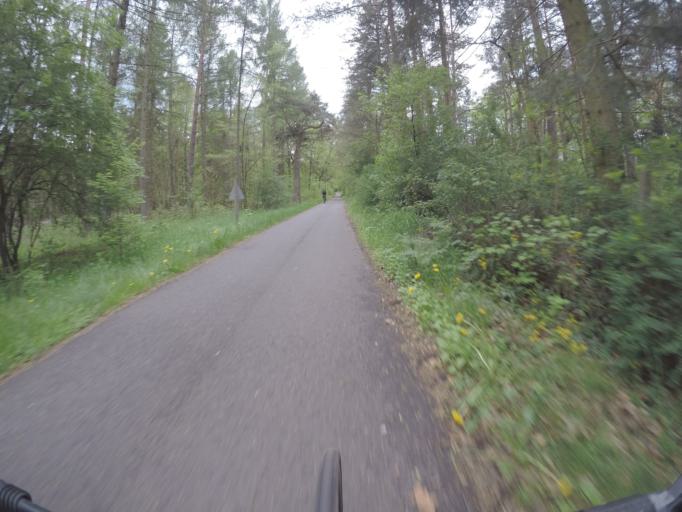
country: DE
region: Brandenburg
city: Marienwerder
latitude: 52.8352
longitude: 13.6259
